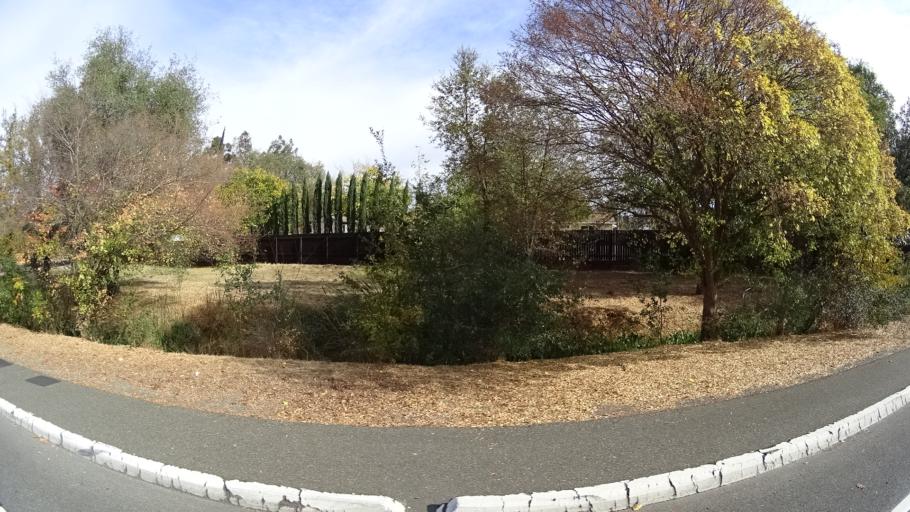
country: US
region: California
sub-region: Sacramento County
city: Citrus Heights
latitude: 38.7073
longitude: -121.2627
